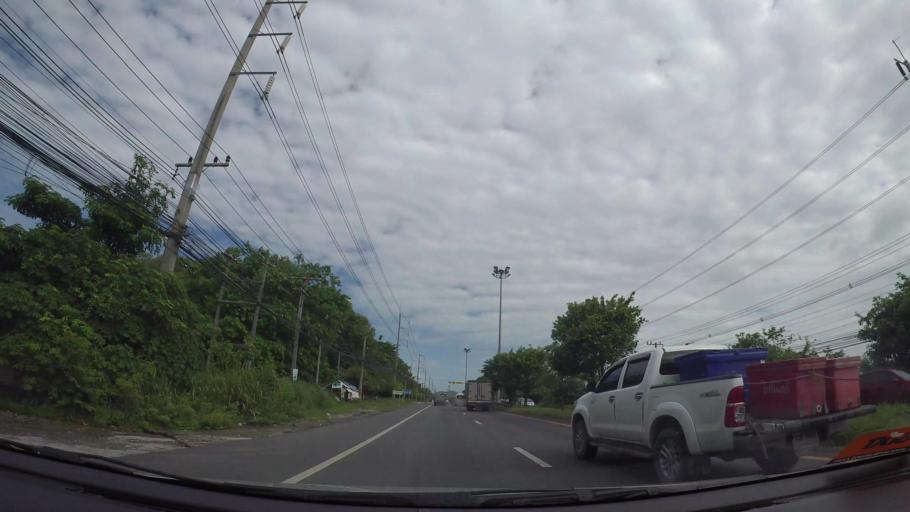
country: TH
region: Rayong
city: Ban Chang
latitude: 12.7199
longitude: 101.1571
